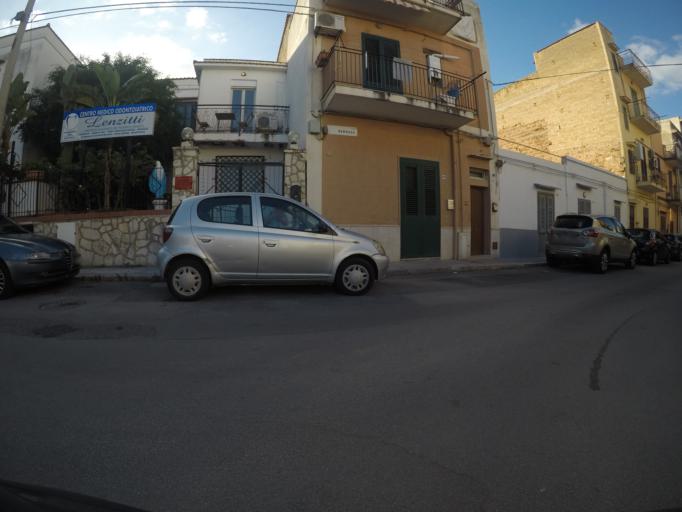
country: IT
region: Sicily
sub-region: Palermo
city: Isola delle Femmine
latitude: 38.2007
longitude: 13.2795
